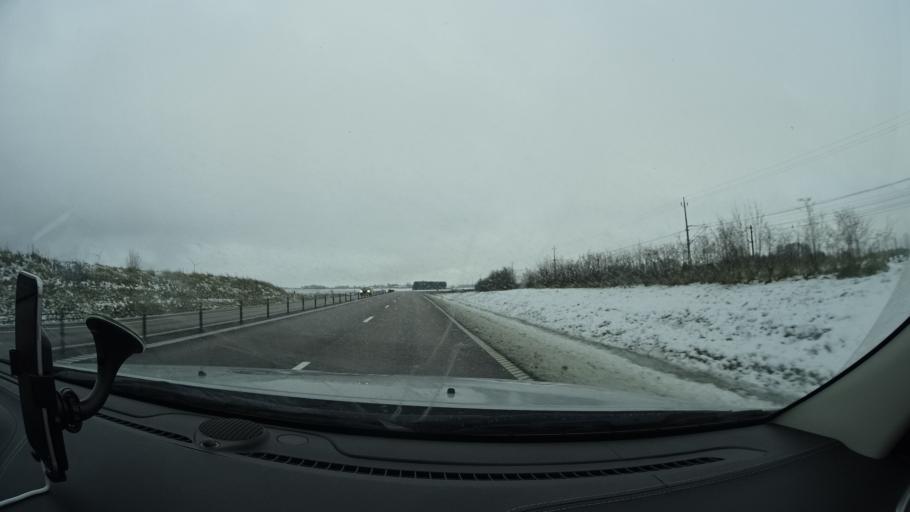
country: SE
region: OEstergoetland
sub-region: Motala Kommun
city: Stenstorp
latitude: 58.4841
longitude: 15.0298
